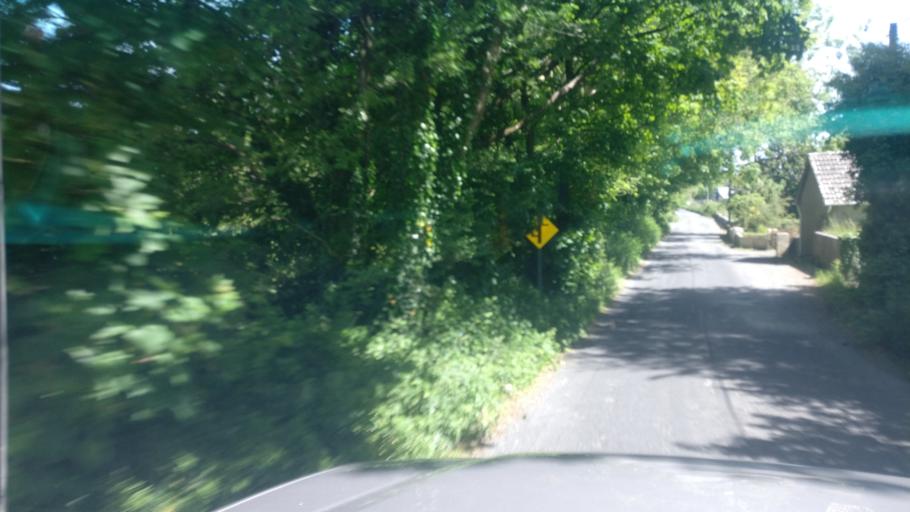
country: IE
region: Connaught
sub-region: County Galway
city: Gort
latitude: 53.1519
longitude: -8.7546
